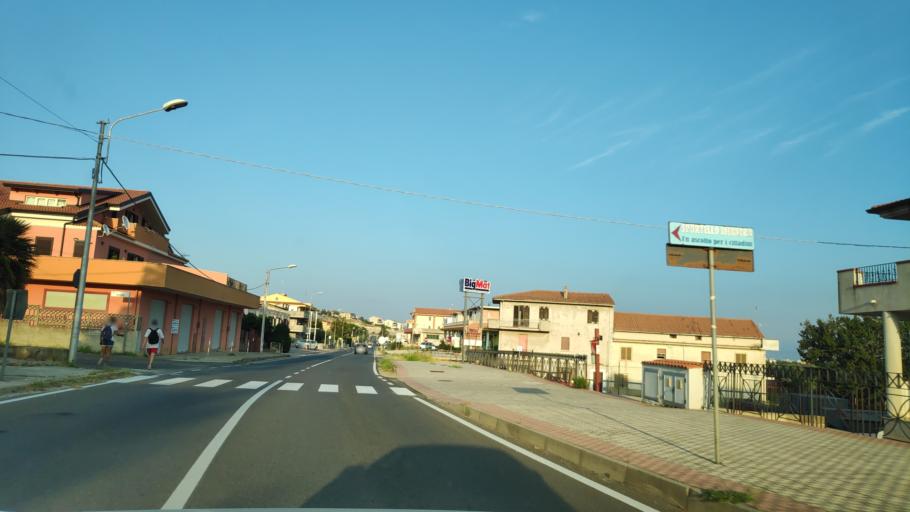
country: IT
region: Calabria
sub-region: Provincia di Catanzaro
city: Martelli-Laganosa
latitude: 38.6792
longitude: 16.5276
